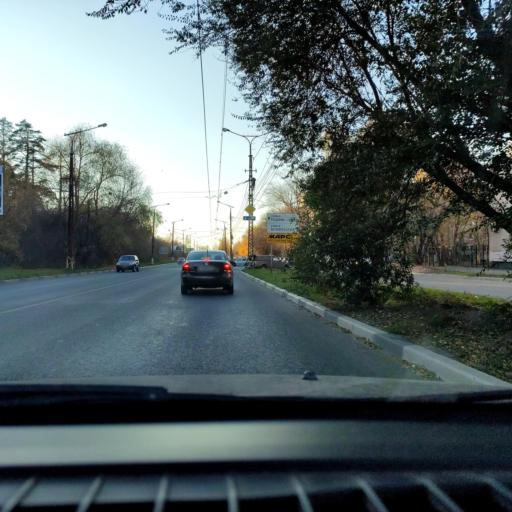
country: RU
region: Samara
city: Tol'yatti
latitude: 53.4984
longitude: 49.3973
